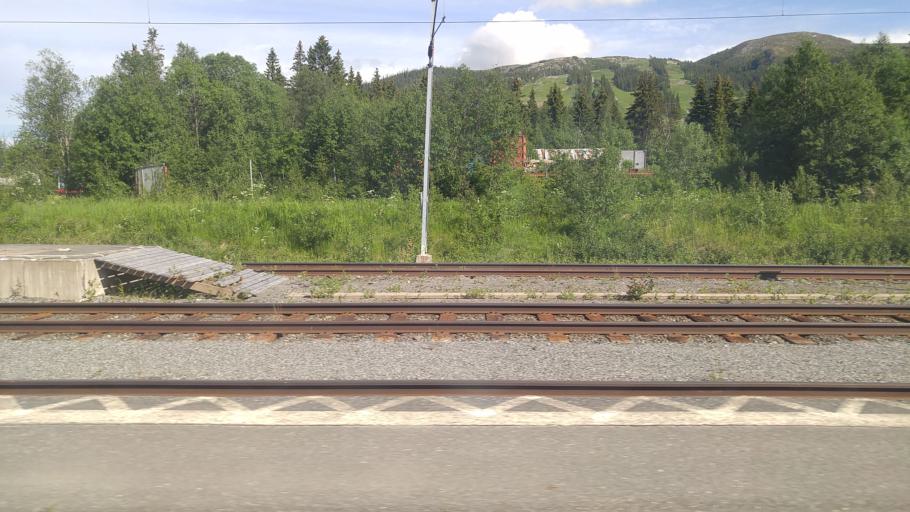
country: SE
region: Jaemtland
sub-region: Are Kommun
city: Are
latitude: 63.3899
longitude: 12.9249
